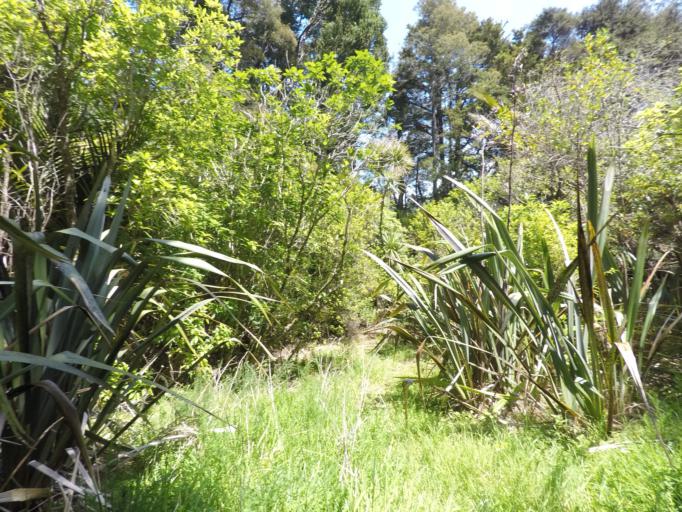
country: NZ
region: Auckland
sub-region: Auckland
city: Titirangi
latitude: -36.9706
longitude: 174.6328
